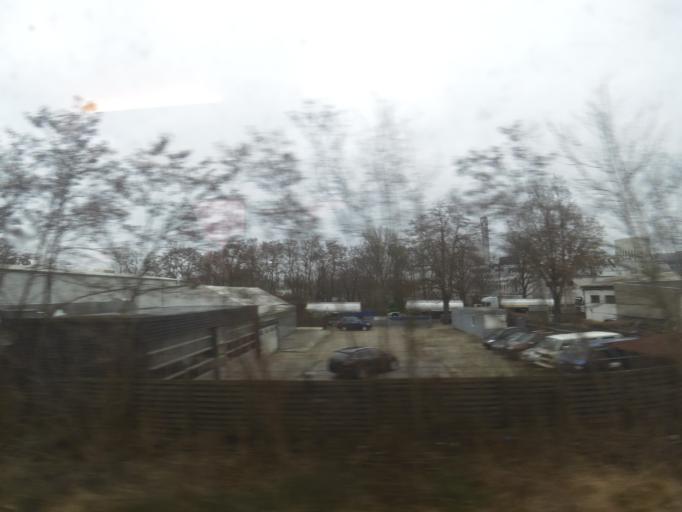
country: DE
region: Berlin
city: Haselhorst
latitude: 52.5296
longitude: 13.2288
